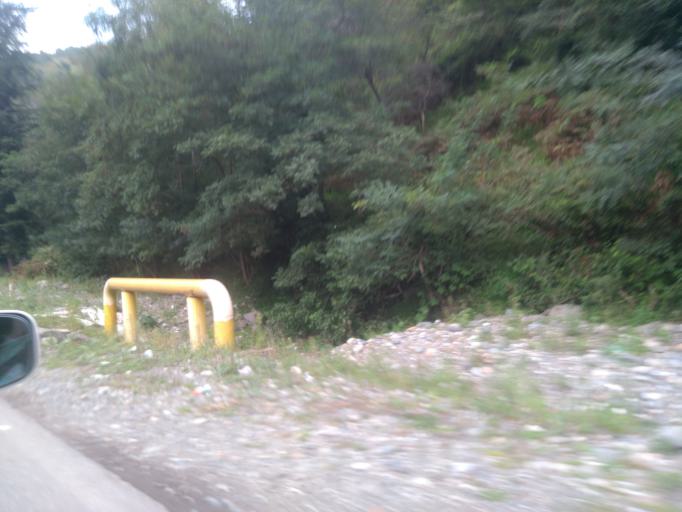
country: GE
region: Ajaria
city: Khelvachauri
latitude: 41.5462
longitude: 41.7061
